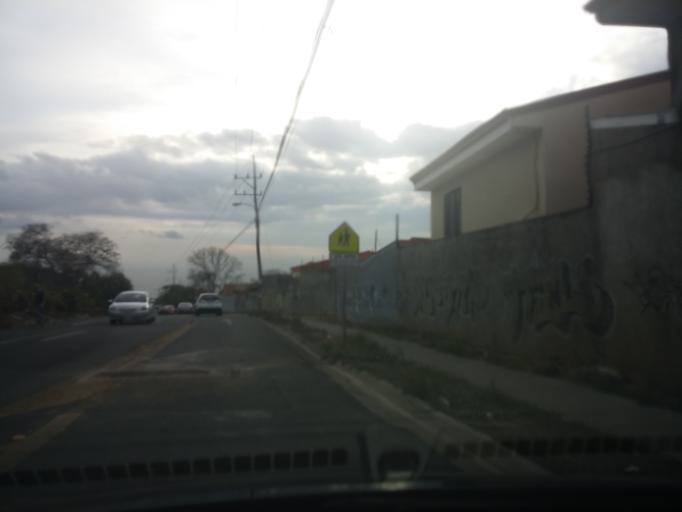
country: CR
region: Heredia
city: San Francisco
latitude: 9.9898
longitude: -84.1417
